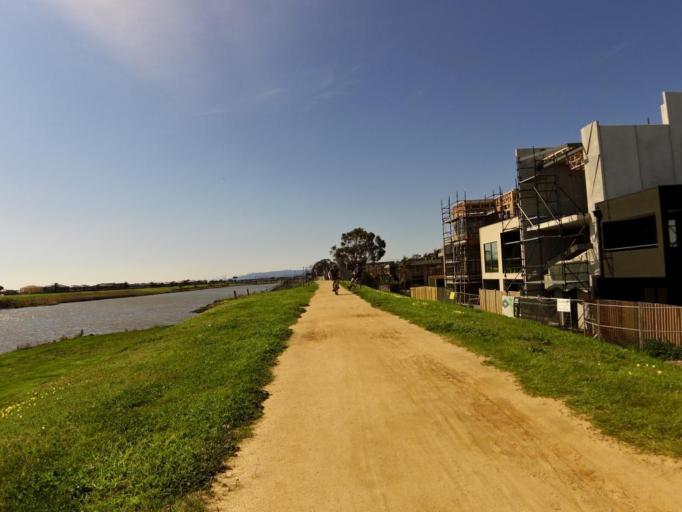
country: AU
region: Victoria
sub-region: Kingston
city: Patterson Lakes
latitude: -38.0658
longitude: 145.1402
